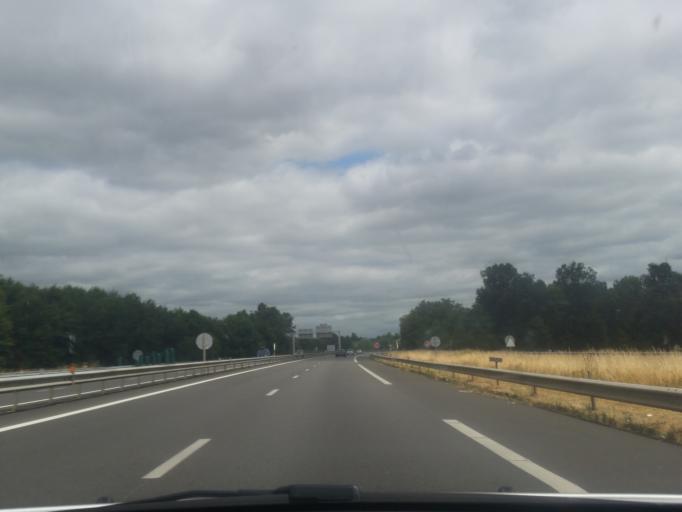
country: FR
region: Pays de la Loire
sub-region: Departement de Maine-et-Loire
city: Seiches-sur-le-Loir
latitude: 47.5445
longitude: -0.3399
